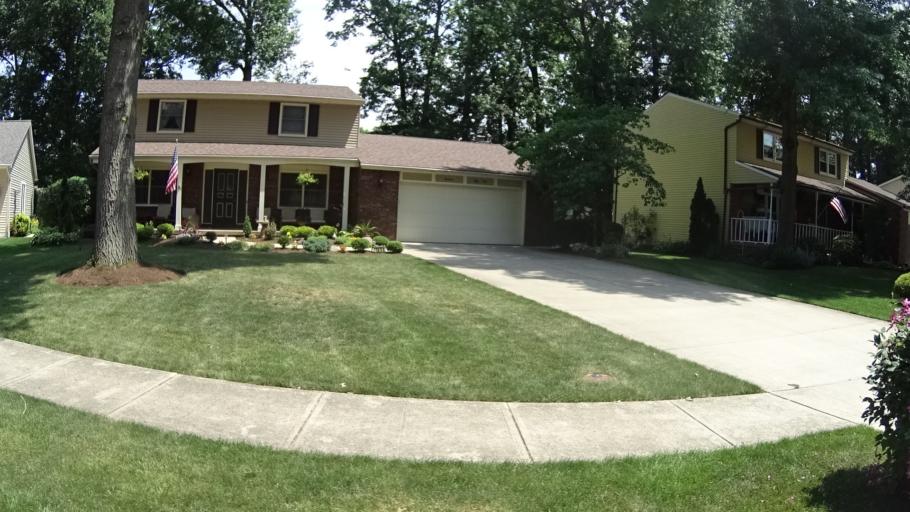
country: US
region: Ohio
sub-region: Lorain County
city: Vermilion
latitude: 41.4069
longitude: -82.3568
